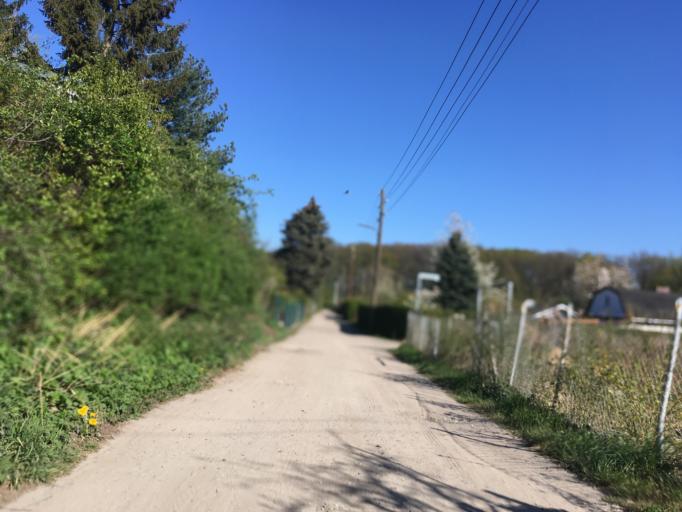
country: DE
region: Berlin
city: Rosenthal
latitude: 52.6014
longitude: 13.3929
